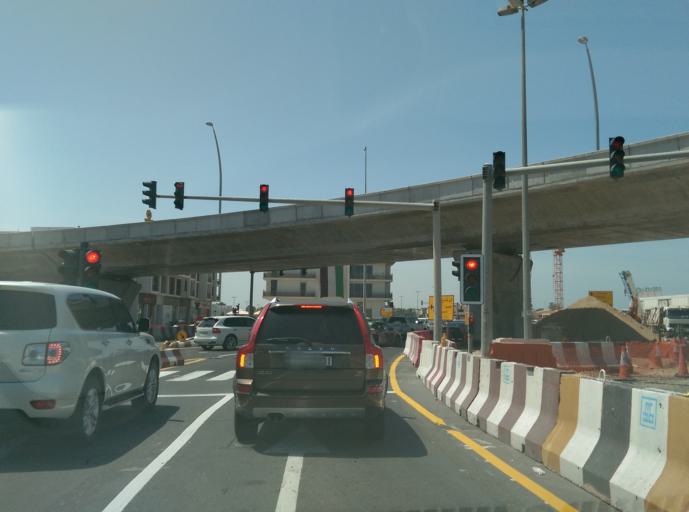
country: AE
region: Dubai
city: Dubai
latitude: 25.1872
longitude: 55.2403
